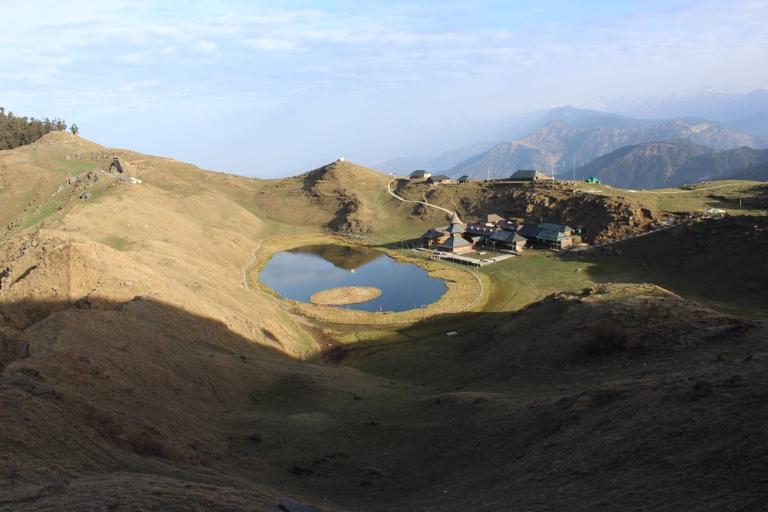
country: IN
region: Himachal Pradesh
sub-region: Mandi
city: Pandoh
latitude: 31.7536
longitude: 77.1014
